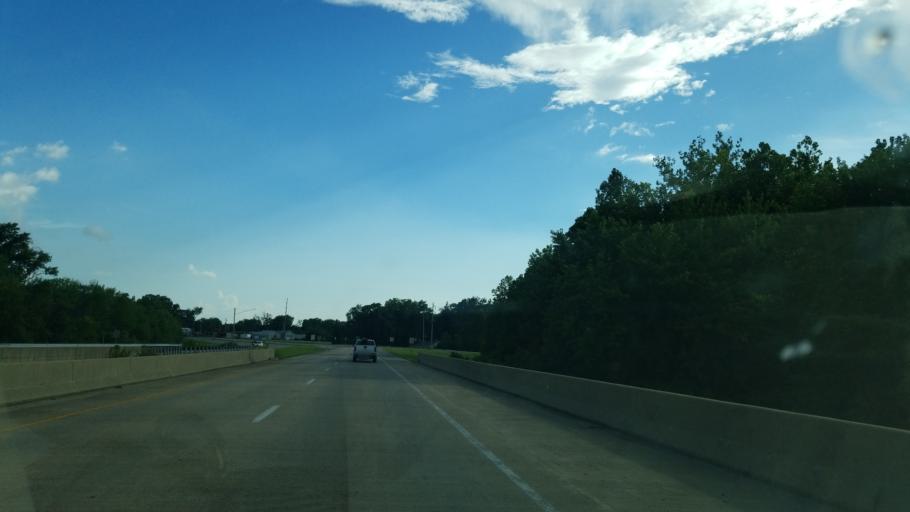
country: US
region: Illinois
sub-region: Marion County
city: Central City
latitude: 38.5564
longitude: -89.1271
